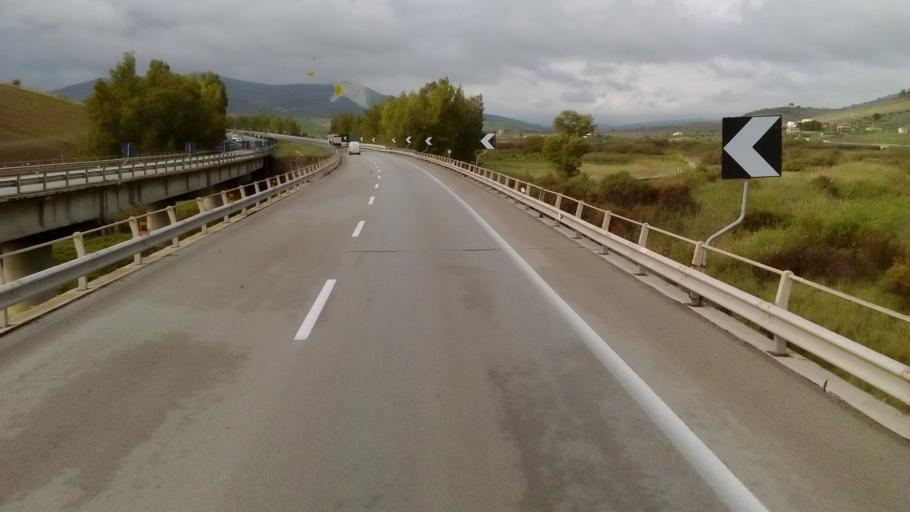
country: IT
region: Sicily
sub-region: Enna
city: Assoro
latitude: 37.5765
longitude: 14.4388
